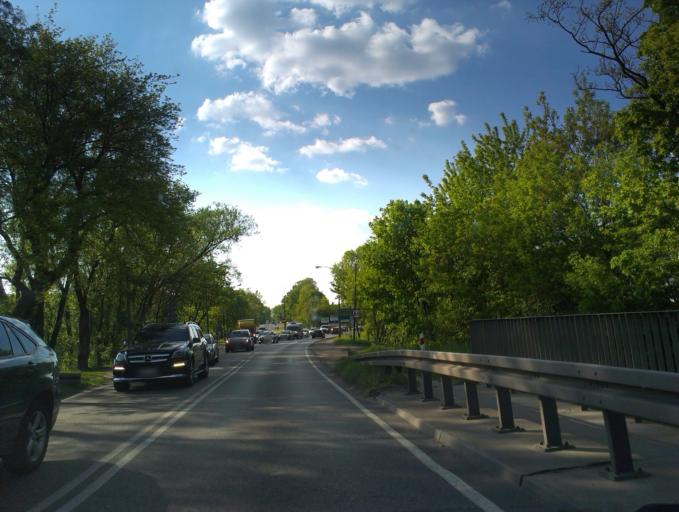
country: PL
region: Masovian Voivodeship
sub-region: Powiat piaseczynski
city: Zabieniec
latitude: 52.0627
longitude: 21.0388
